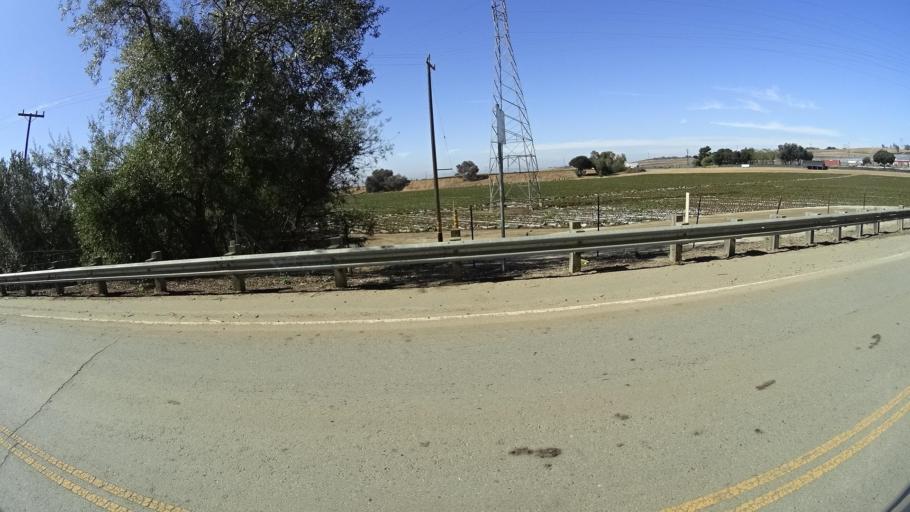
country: US
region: California
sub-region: Monterey County
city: Prunedale
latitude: 36.7713
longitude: -121.6024
